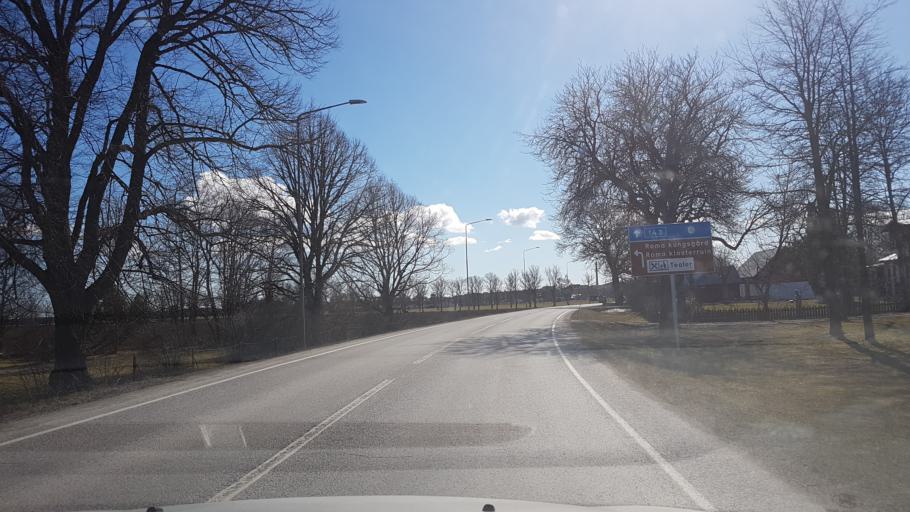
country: SE
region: Gotland
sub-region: Gotland
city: Visby
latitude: 57.5170
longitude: 18.4443
